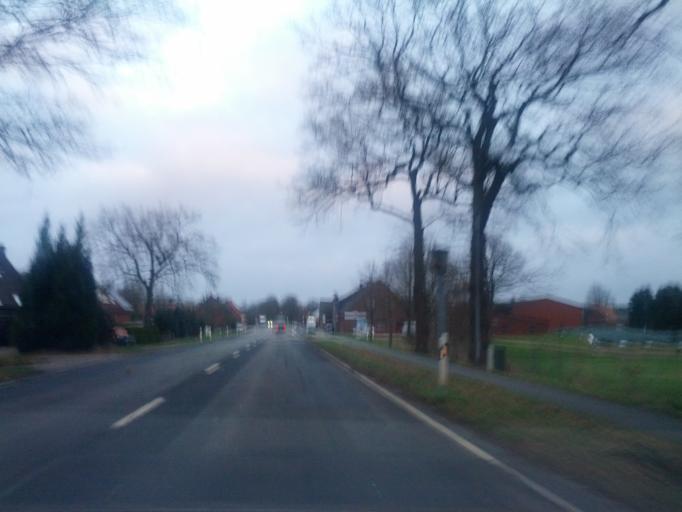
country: DE
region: Lower Saxony
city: Wistedt
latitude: 53.2695
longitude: 9.6790
